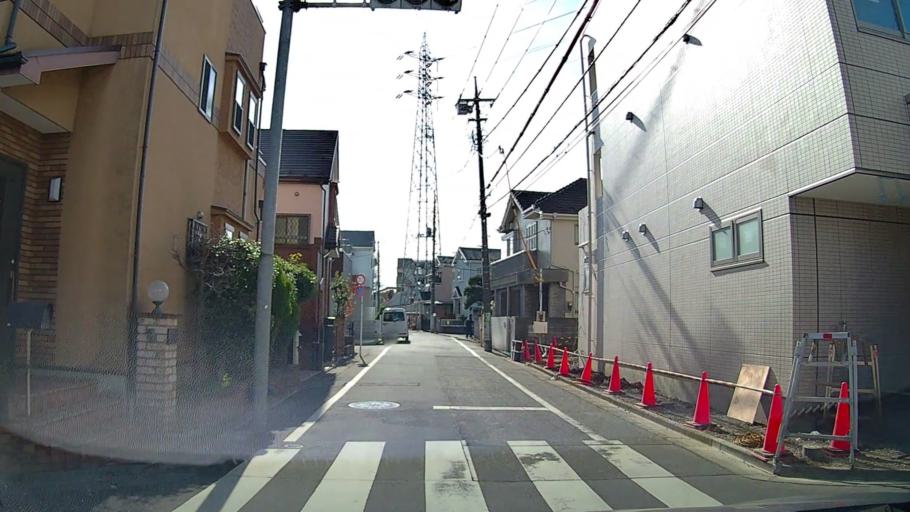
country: JP
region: Saitama
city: Wako
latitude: 35.7578
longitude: 139.6180
